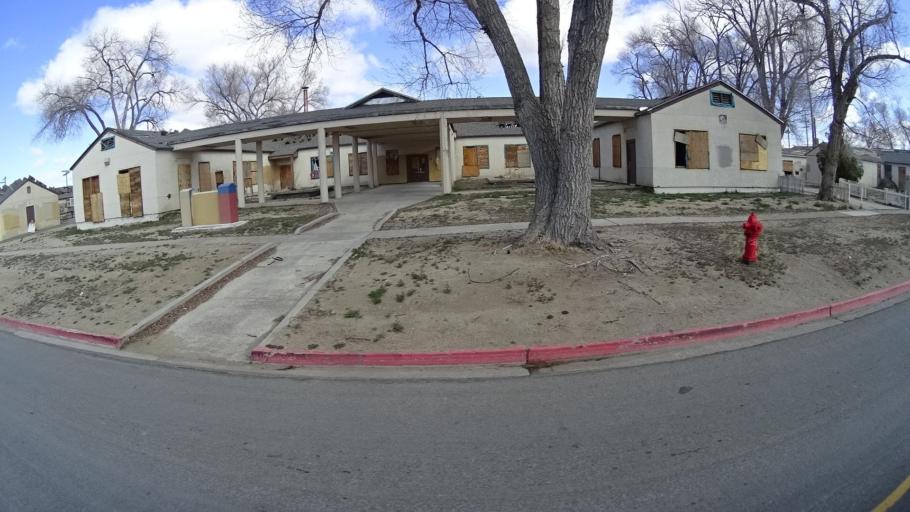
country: US
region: Nevada
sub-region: Washoe County
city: Lemmon Valley
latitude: 39.6538
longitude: -119.8755
